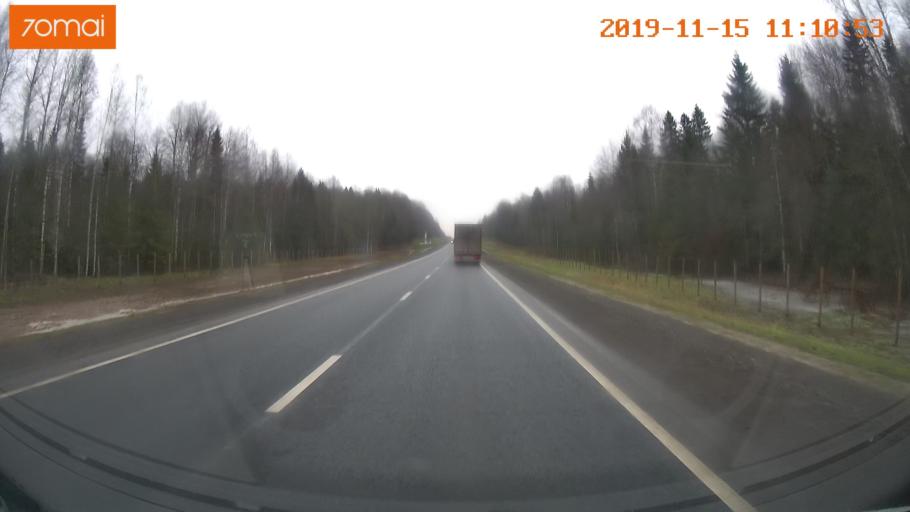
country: RU
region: Vologda
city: Chebsara
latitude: 59.1211
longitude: 39.1314
